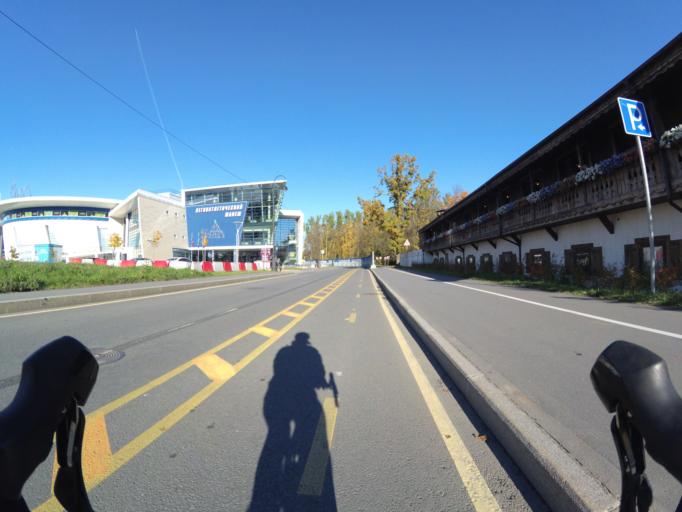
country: RU
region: St.-Petersburg
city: Staraya Derevnya
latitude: 59.9703
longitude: 30.2314
